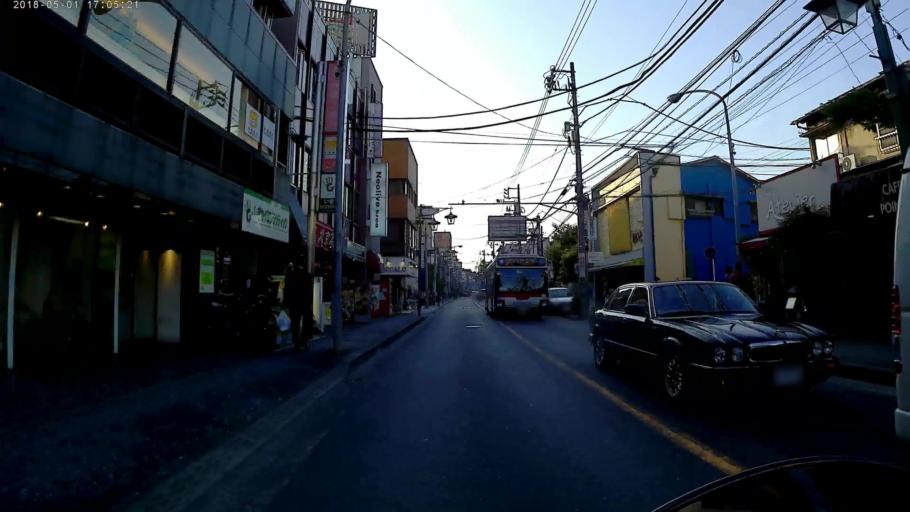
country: JP
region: Kanagawa
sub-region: Kawasaki-shi
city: Kawasaki
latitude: 35.5372
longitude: 139.6318
